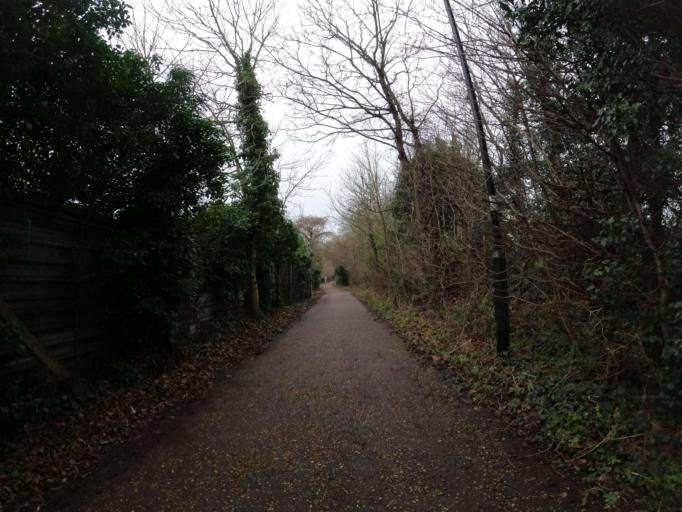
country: GB
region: England
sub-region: Greater London
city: Greenford
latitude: 51.5162
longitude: -0.3437
